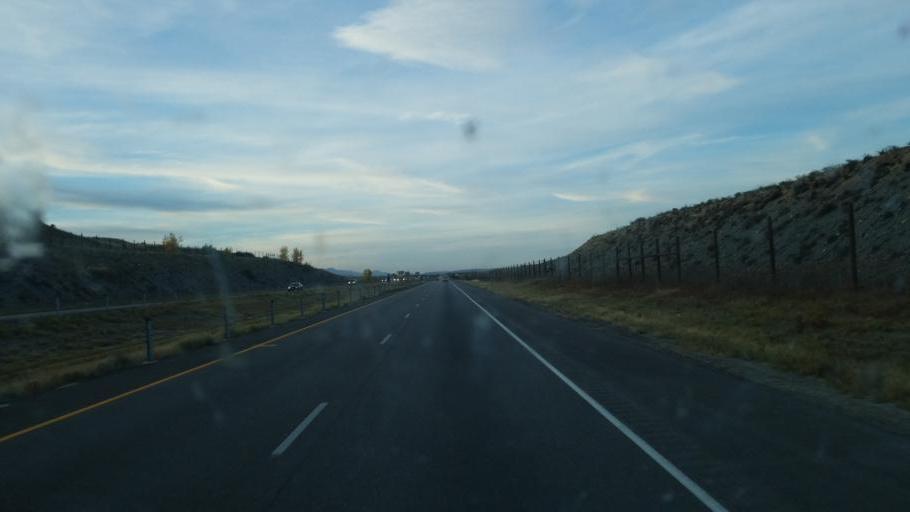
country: US
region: Colorado
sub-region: El Paso County
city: Fountain
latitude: 38.6472
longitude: -104.6950
